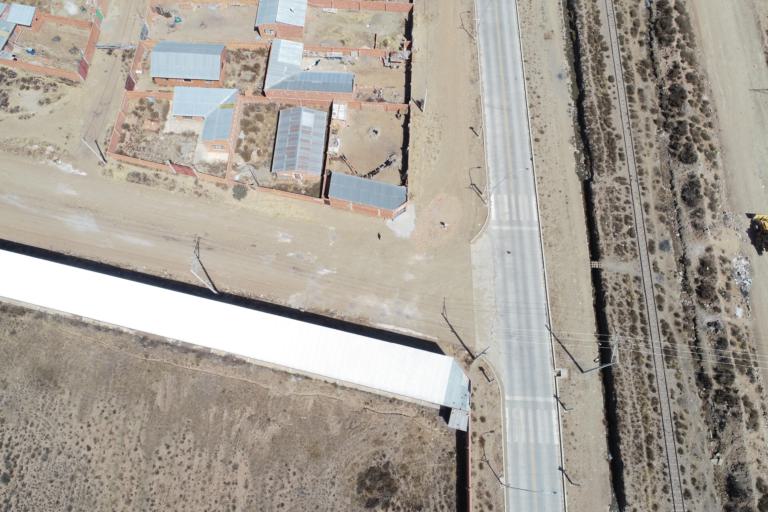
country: BO
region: La Paz
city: La Paz
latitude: -16.5905
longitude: -68.2121
